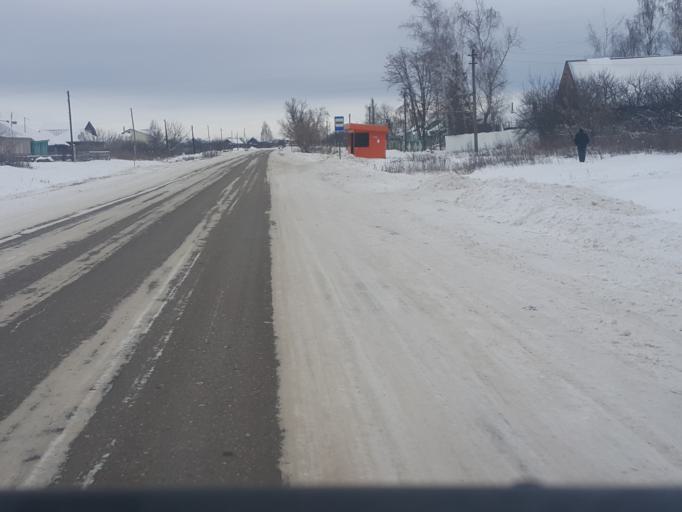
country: RU
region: Tambov
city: Platonovka
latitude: 52.8413
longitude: 41.8124
